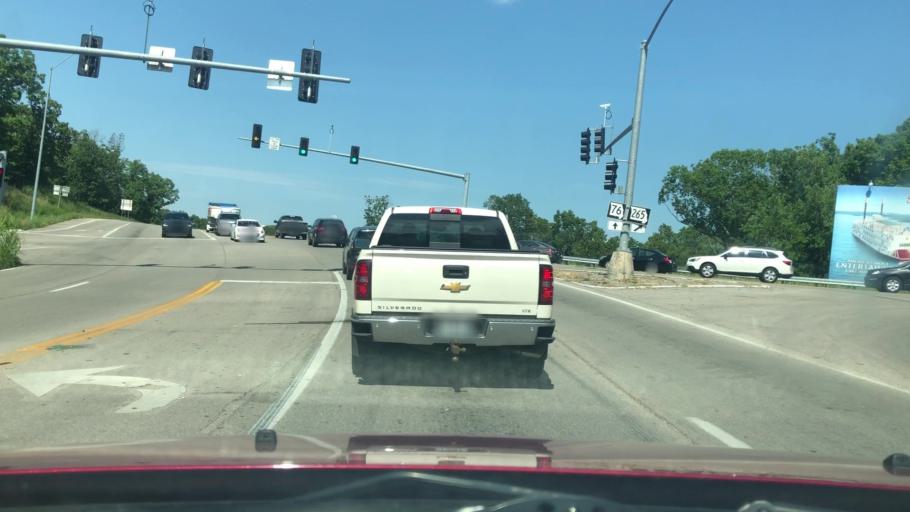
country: US
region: Missouri
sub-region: Stone County
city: Kimberling City
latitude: 36.6751
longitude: -93.3267
